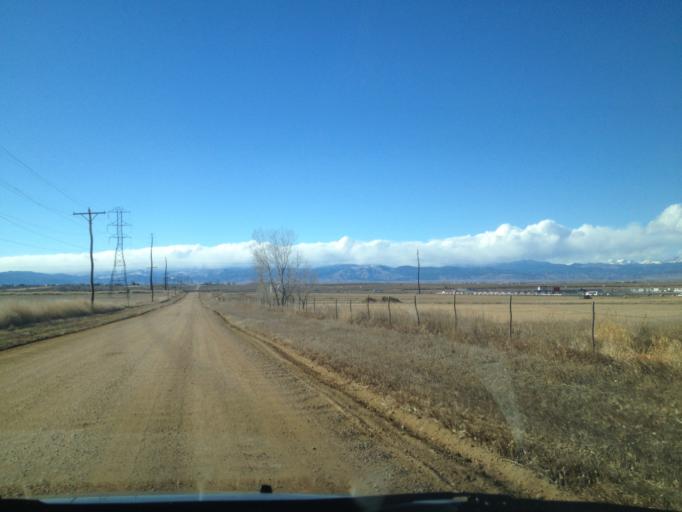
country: US
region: Colorado
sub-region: Weld County
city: Dacono
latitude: 40.0586
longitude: -104.9649
